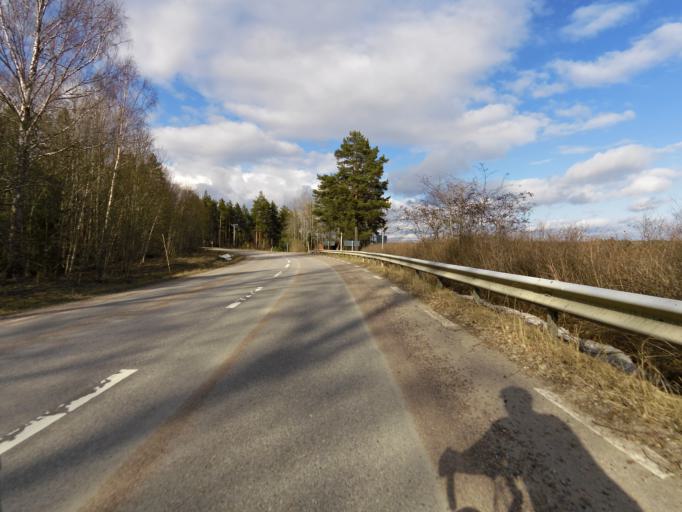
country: SE
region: Dalarna
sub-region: Avesta Kommun
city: Horndal
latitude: 60.4716
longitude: 16.4568
